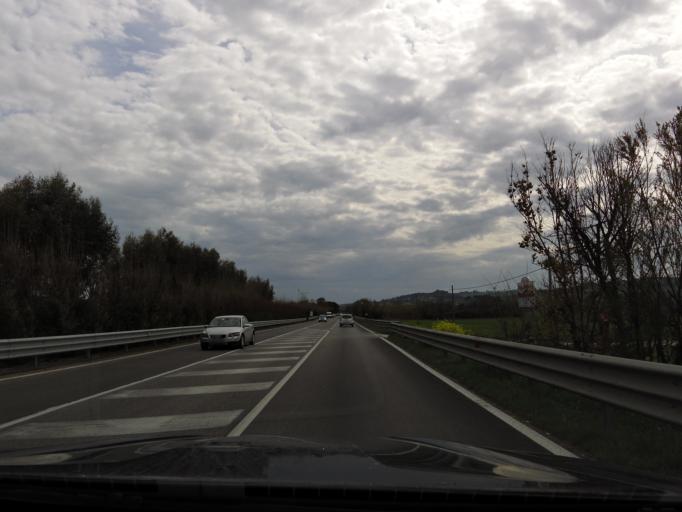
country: IT
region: The Marches
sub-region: Provincia di Macerata
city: Porto Recanati
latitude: 43.4005
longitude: 13.6784
